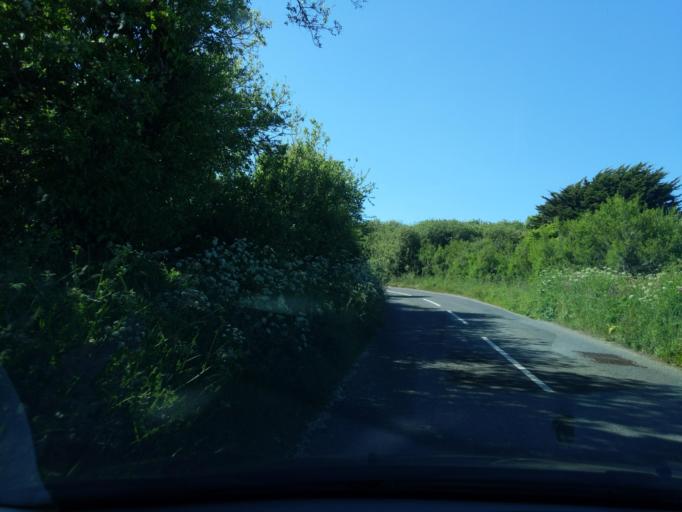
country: GB
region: England
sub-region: Cornwall
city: St. Buryan
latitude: 50.0601
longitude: -5.6267
